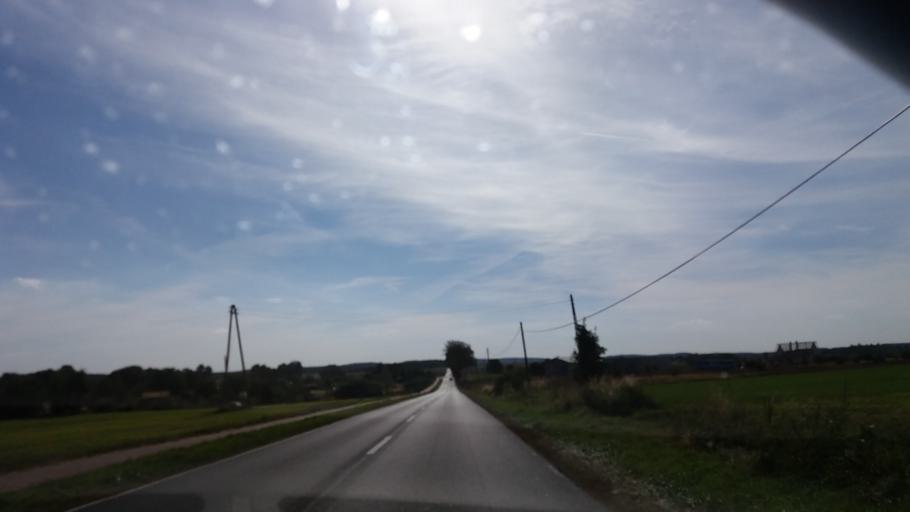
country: PL
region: Lubusz
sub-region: Powiat strzelecko-drezdenecki
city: Dobiegniew
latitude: 52.9604
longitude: 15.7510
